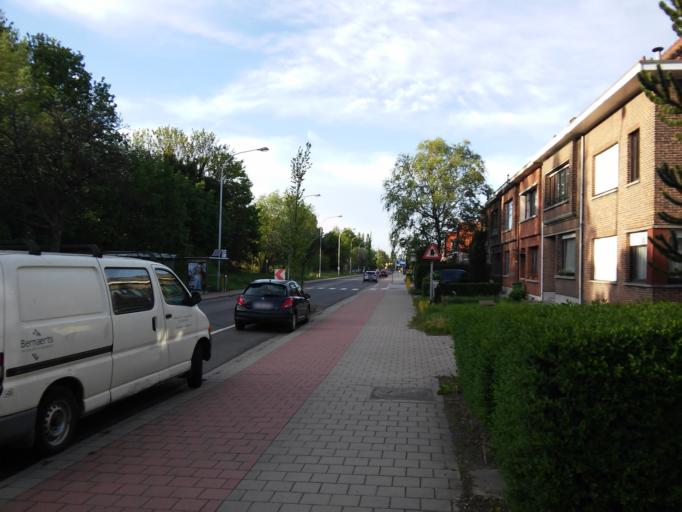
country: BE
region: Flanders
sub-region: Provincie Antwerpen
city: Hemiksem
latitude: 51.1532
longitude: 4.3421
